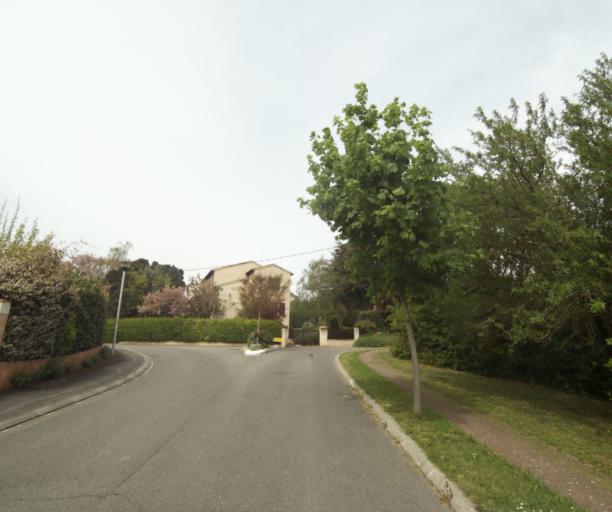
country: FR
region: Midi-Pyrenees
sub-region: Departement de la Haute-Garonne
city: Pechabou
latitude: 43.5044
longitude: 1.5028
